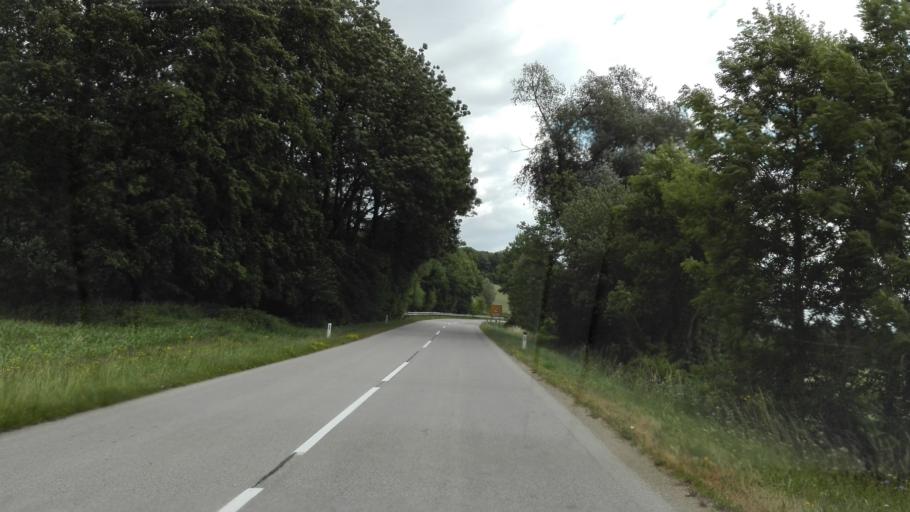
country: AT
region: Upper Austria
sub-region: Politischer Bezirk Perg
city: Perg
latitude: 48.2351
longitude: 14.6665
